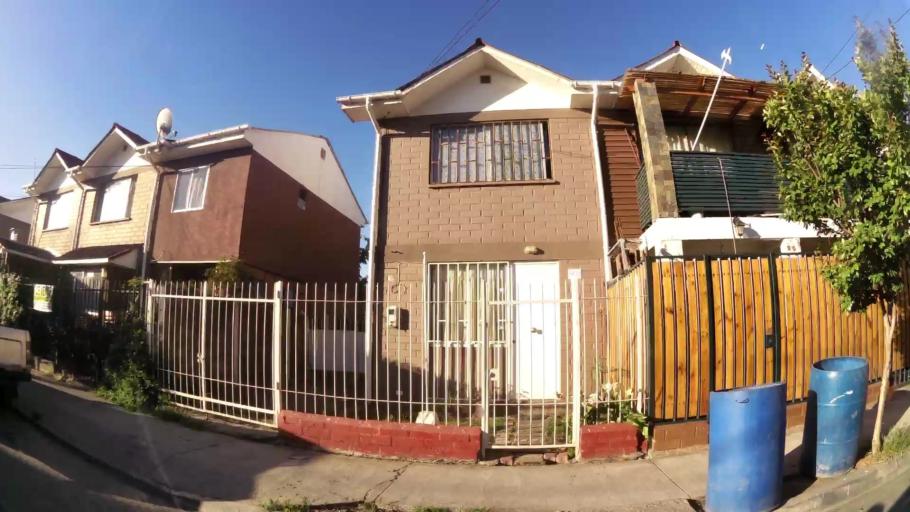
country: CL
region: Santiago Metropolitan
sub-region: Provincia de Maipo
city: San Bernardo
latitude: -33.6029
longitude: -70.6699
